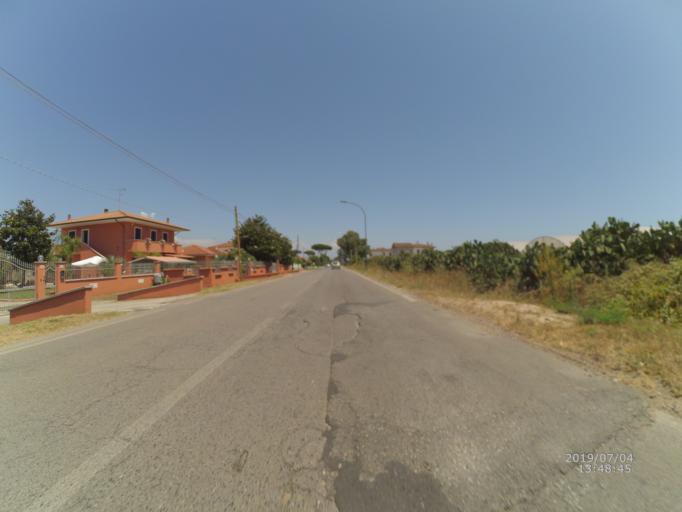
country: IT
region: Latium
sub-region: Provincia di Latina
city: San Felice Circeo
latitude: 41.2850
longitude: 13.1081
